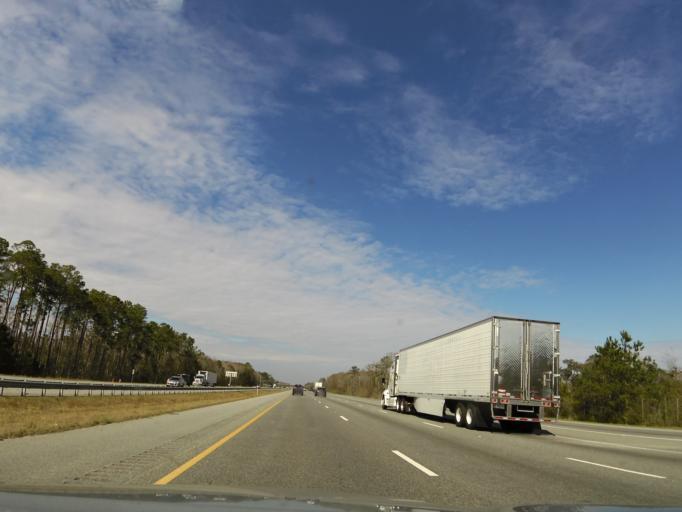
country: US
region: Georgia
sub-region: McIntosh County
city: Darien
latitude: 31.4839
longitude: -81.4472
